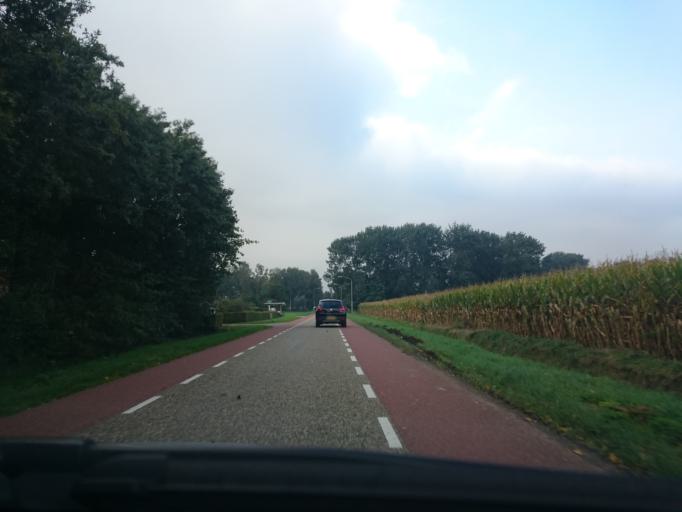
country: NL
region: North Brabant
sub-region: Gemeente Landerd
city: Reek
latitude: 51.7521
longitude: 5.6808
